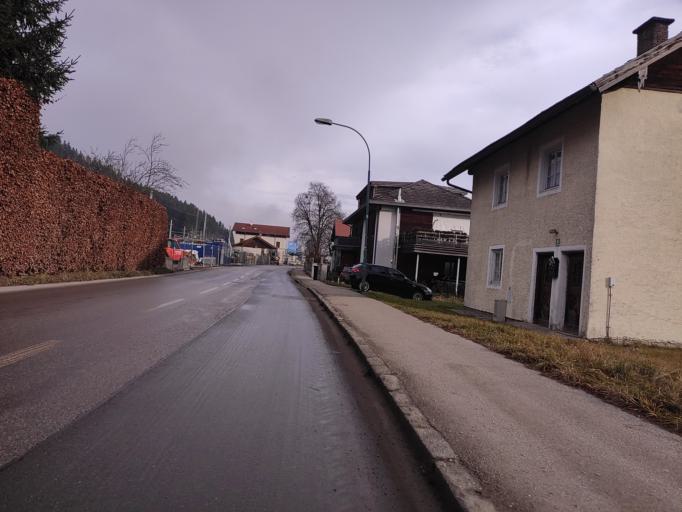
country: AT
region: Salzburg
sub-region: Politischer Bezirk Salzburg-Umgebung
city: Neumarkt am Wallersee
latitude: 47.9533
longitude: 13.2240
